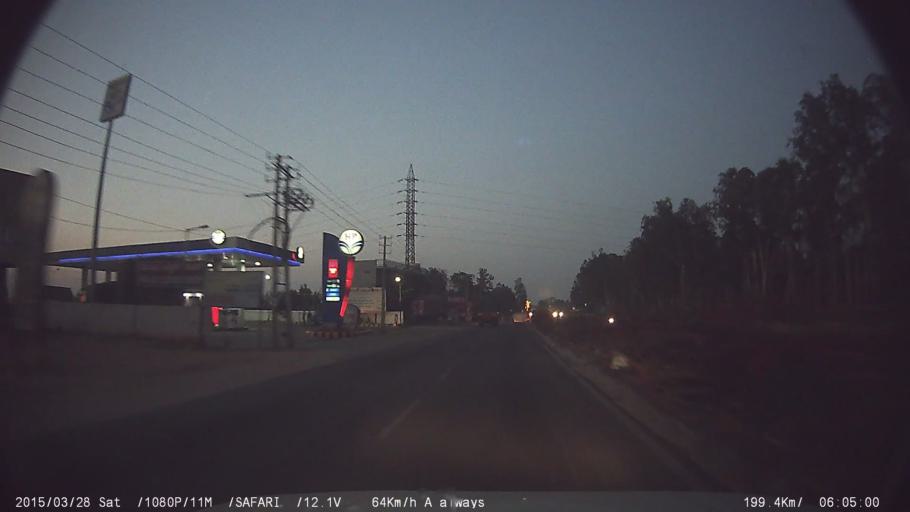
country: IN
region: Karnataka
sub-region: Ramanagara
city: Ramanagaram
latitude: 12.8278
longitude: 77.4121
